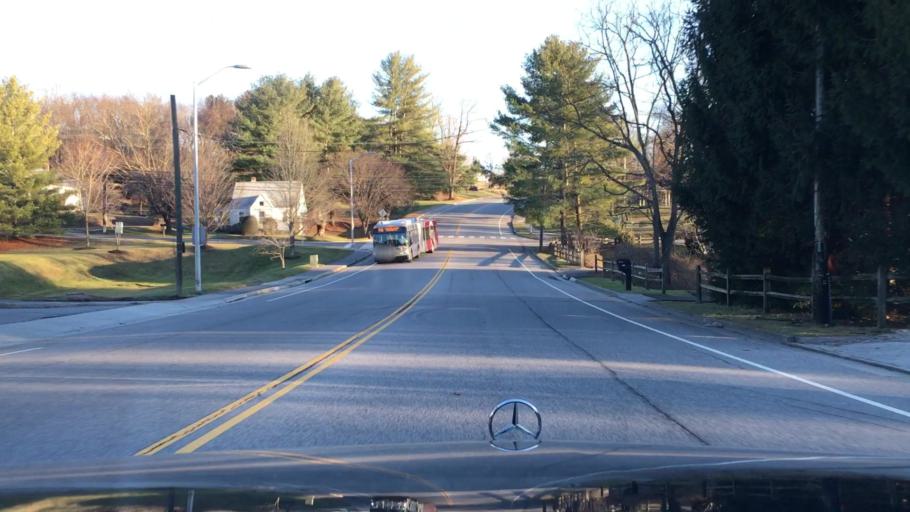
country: US
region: Virginia
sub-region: Montgomery County
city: Blacksburg
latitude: 37.2454
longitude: -80.4131
